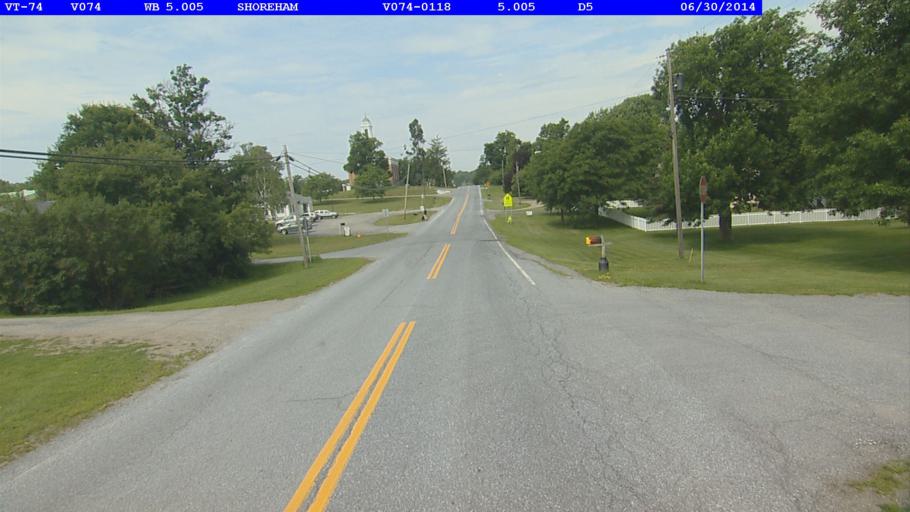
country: US
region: New York
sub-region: Essex County
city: Ticonderoga
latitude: 43.8939
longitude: -73.3139
